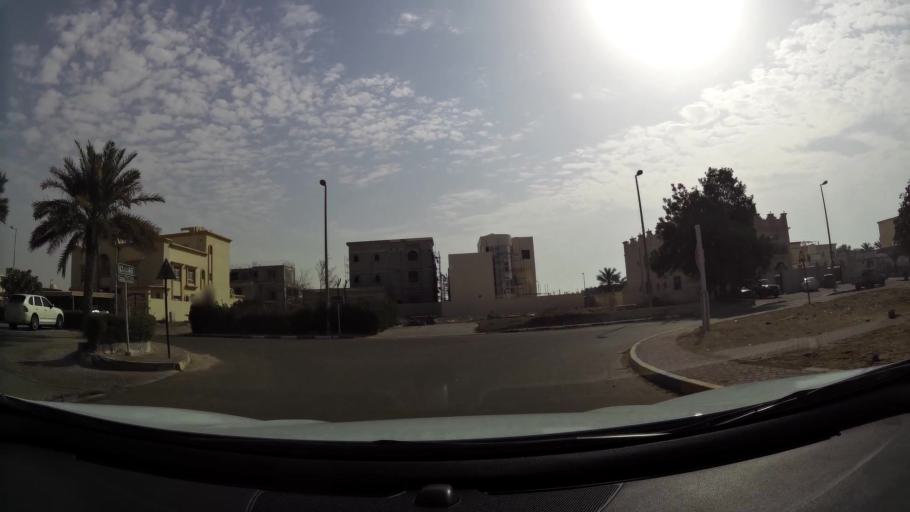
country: AE
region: Abu Dhabi
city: Abu Dhabi
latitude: 24.2662
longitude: 54.6935
